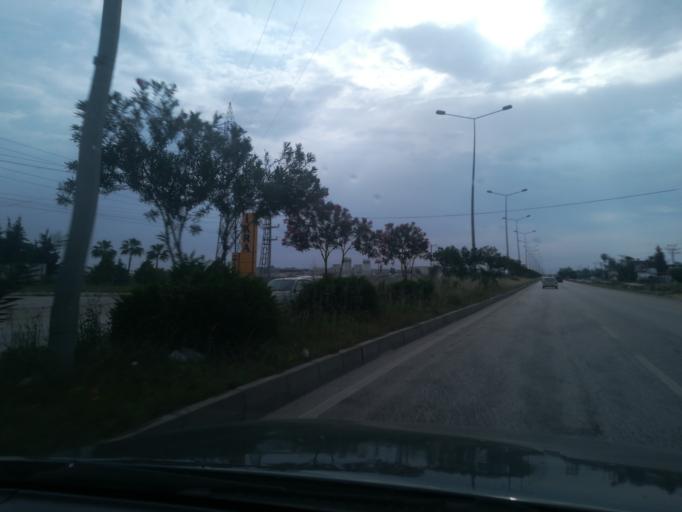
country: TR
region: Adana
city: Yuregir
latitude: 36.9827
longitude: 35.4109
